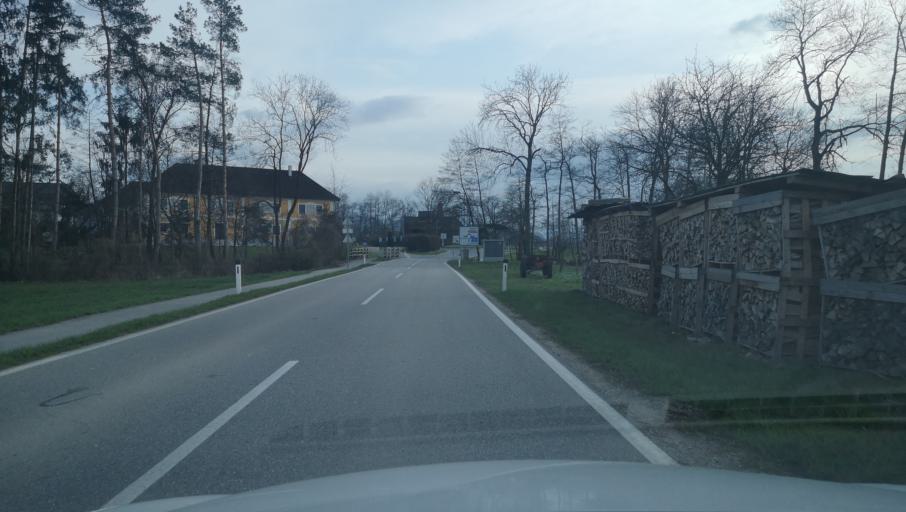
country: AT
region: Lower Austria
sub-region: Politischer Bezirk Amstetten
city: Euratsfeld
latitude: 48.0944
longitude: 14.9271
